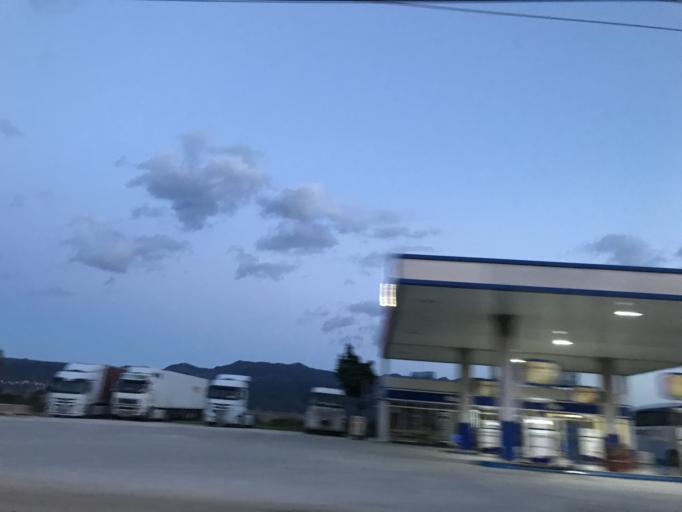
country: TR
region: Hatay
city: Karacay
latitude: 36.1460
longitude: 36.0783
